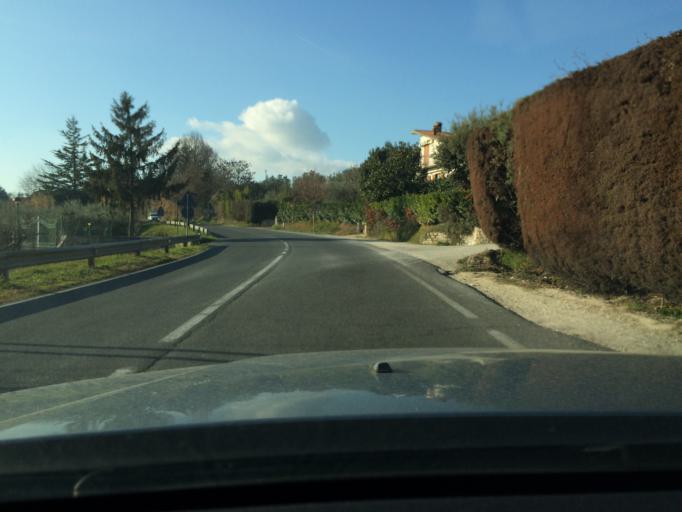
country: IT
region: Umbria
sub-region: Provincia di Terni
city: Amelia
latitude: 42.5582
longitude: 12.4377
